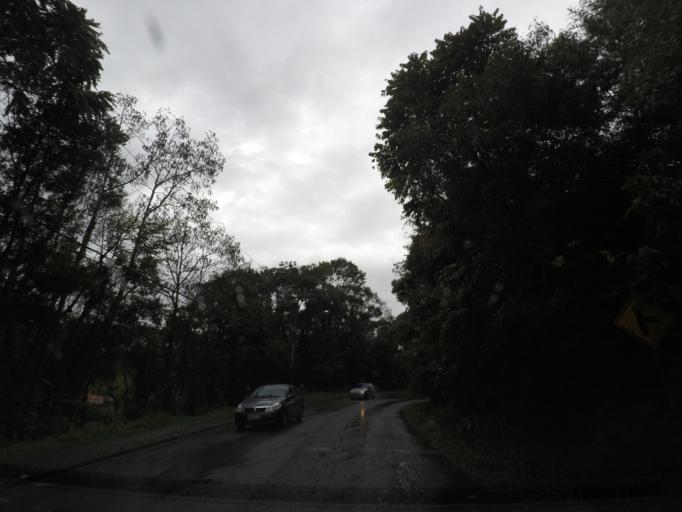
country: BR
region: Parana
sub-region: Curitiba
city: Curitiba
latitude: -25.4625
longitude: -49.3982
